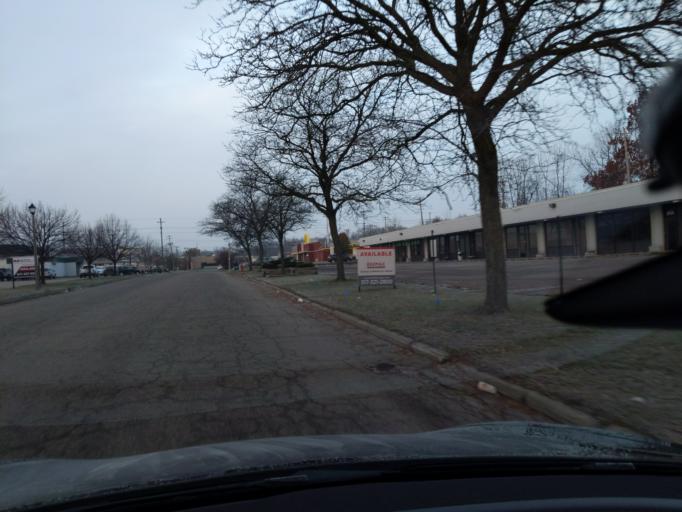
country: US
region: Michigan
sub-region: Ingham County
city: Lansing
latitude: 42.7000
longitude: -84.5649
